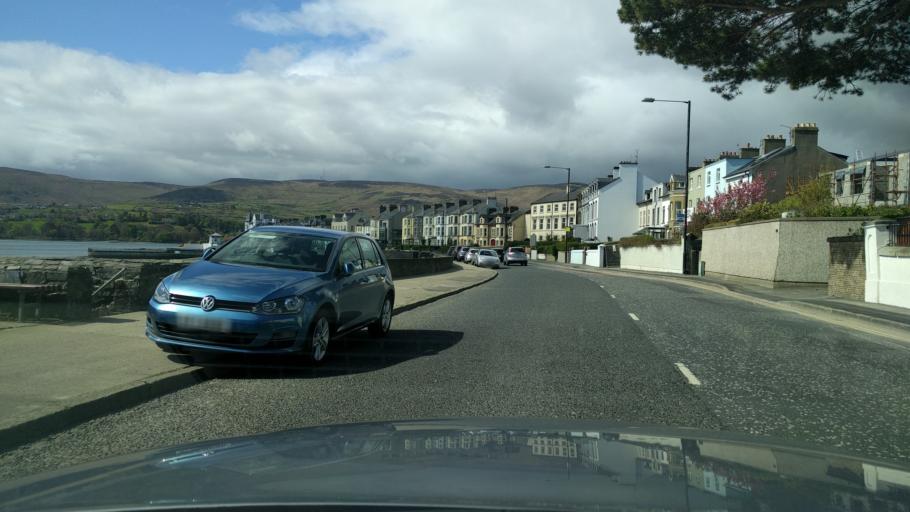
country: GB
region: Northern Ireland
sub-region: Down District
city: Warrenpoint
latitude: 54.0998
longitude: -6.2449
